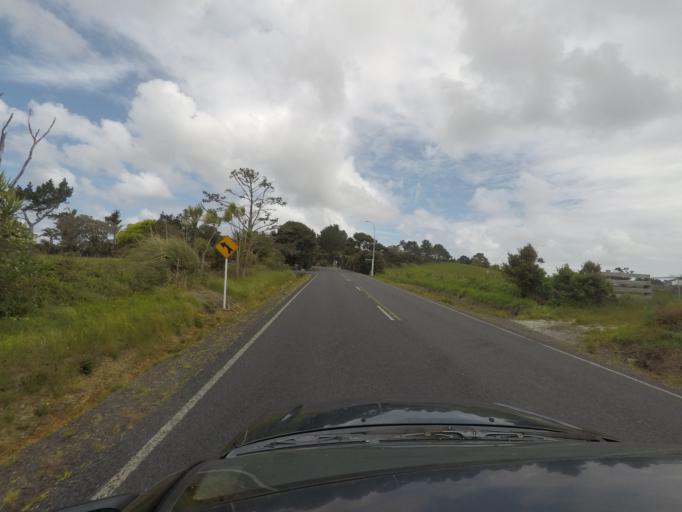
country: NZ
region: Auckland
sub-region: Auckland
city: Parakai
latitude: -36.6365
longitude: 174.5057
